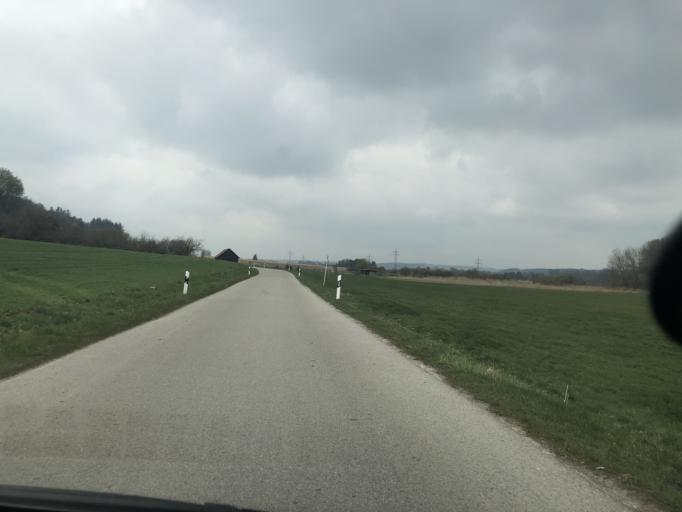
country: DE
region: Bavaria
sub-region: Upper Bavaria
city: Wolfersdorf
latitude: 48.4411
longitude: 11.7183
